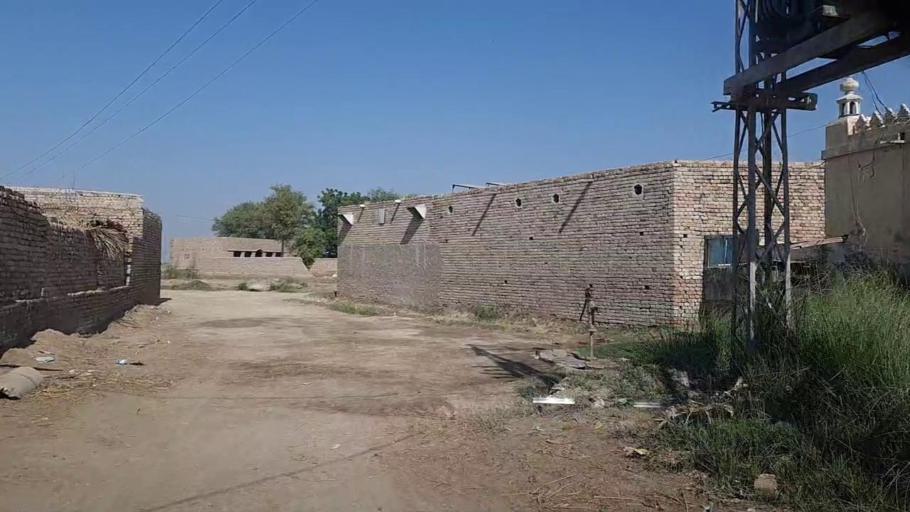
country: PK
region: Sindh
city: Thul
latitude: 28.2180
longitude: 68.7551
